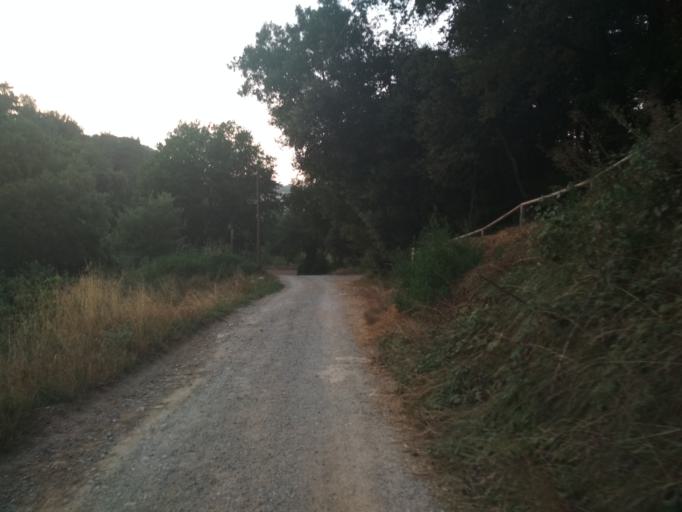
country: ES
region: Catalonia
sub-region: Provincia de Barcelona
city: Castelltercol
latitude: 41.7449
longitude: 2.1194
